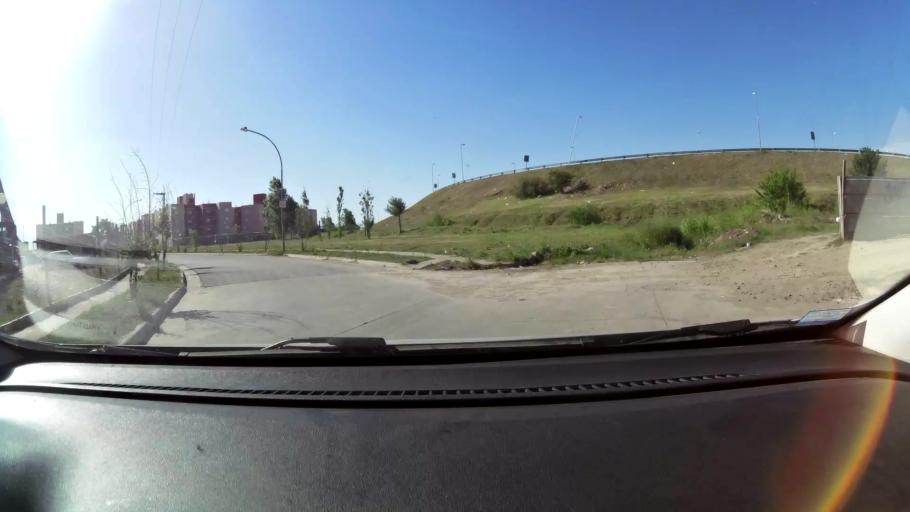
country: AR
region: Cordoba
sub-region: Departamento de Capital
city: Cordoba
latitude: -31.3566
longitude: -64.1890
